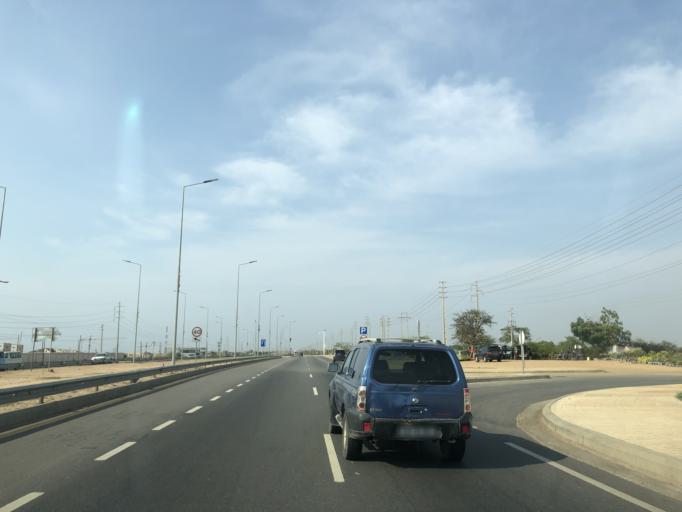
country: AO
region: Luanda
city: Luanda
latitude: -8.9599
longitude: 13.2572
